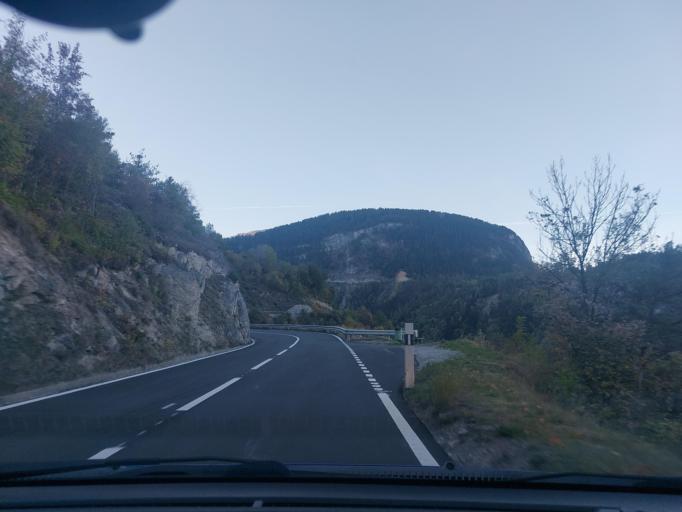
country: CH
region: Valais
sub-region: Sierre District
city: Chippis
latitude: 46.2777
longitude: 7.5491
